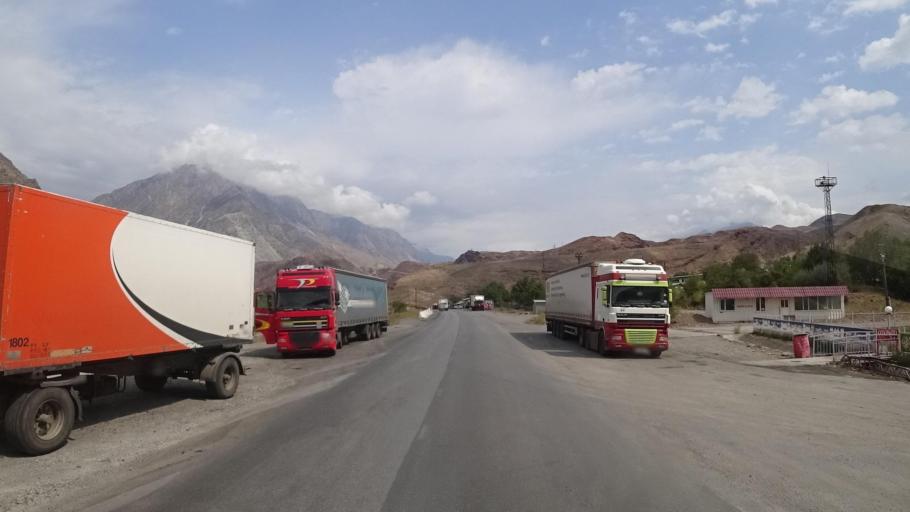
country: KG
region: Jalal-Abad
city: Toktogul
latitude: 41.6137
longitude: 72.6199
